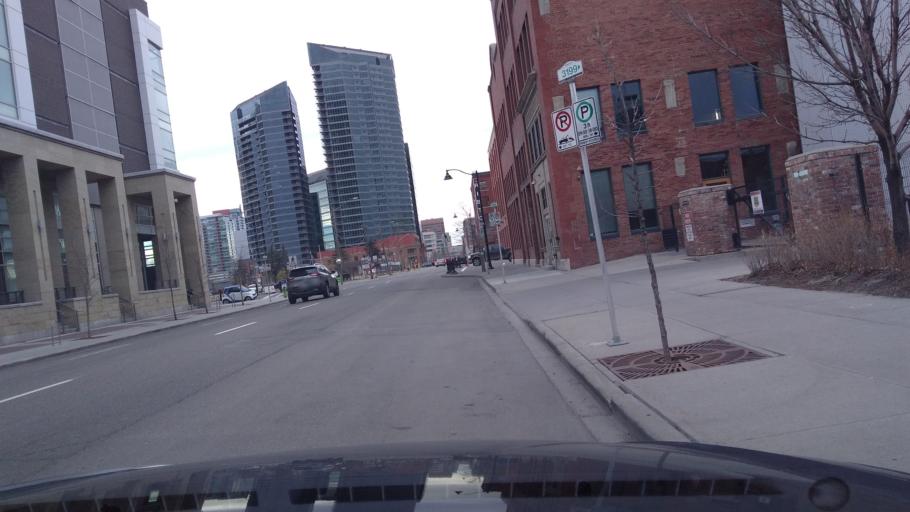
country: CA
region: Alberta
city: Calgary
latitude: 51.0422
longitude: -114.0549
